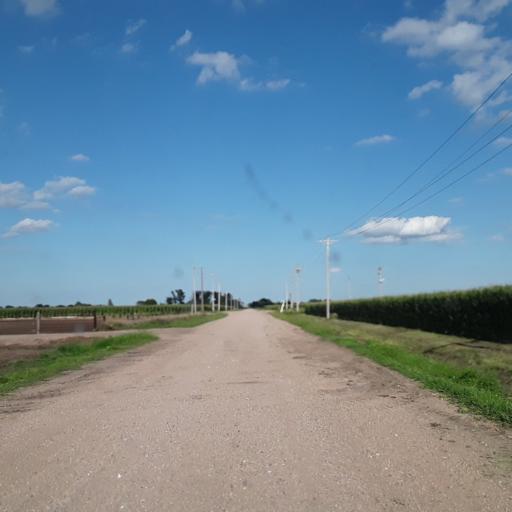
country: US
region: Nebraska
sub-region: Hall County
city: Wood River
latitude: 40.9167
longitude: -98.5717
